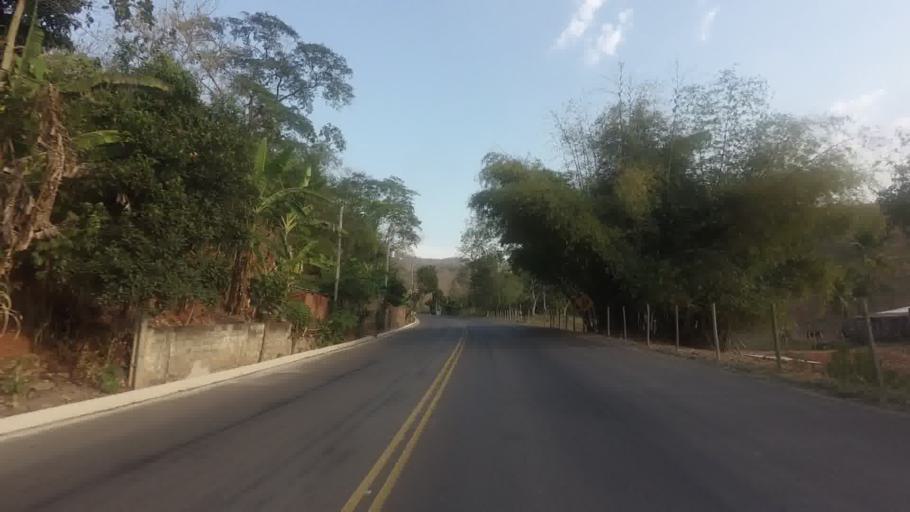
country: BR
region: Rio de Janeiro
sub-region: Cambuci
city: Cambuci
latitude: -21.4515
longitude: -42.0137
